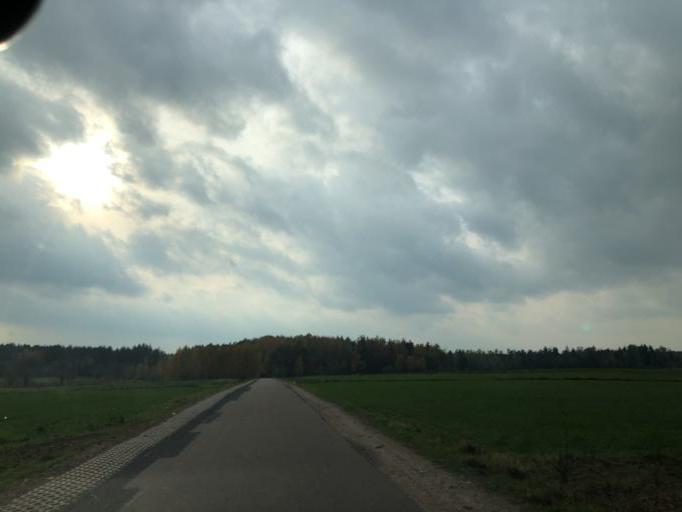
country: PL
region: Podlasie
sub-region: Lomza
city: Lomza
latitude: 53.1428
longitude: 21.9812
